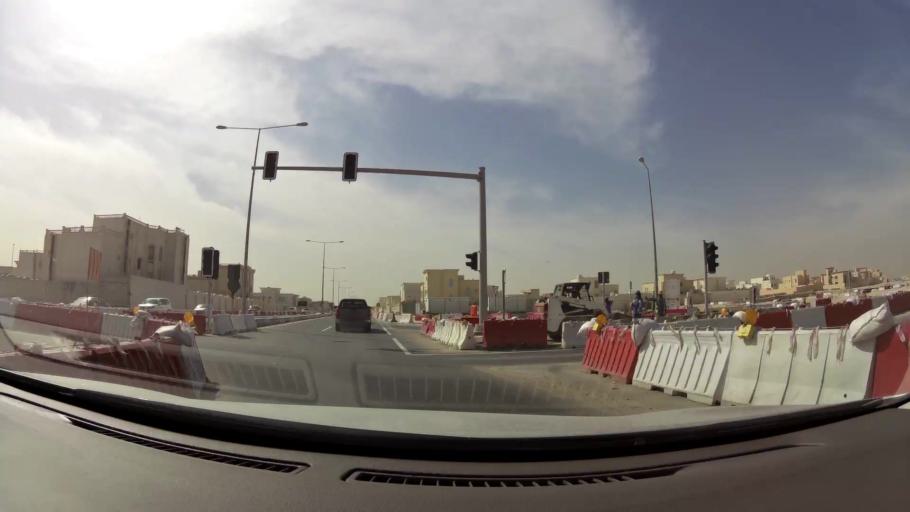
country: QA
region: Baladiyat ar Rayyan
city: Ar Rayyan
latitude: 25.3228
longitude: 51.3947
